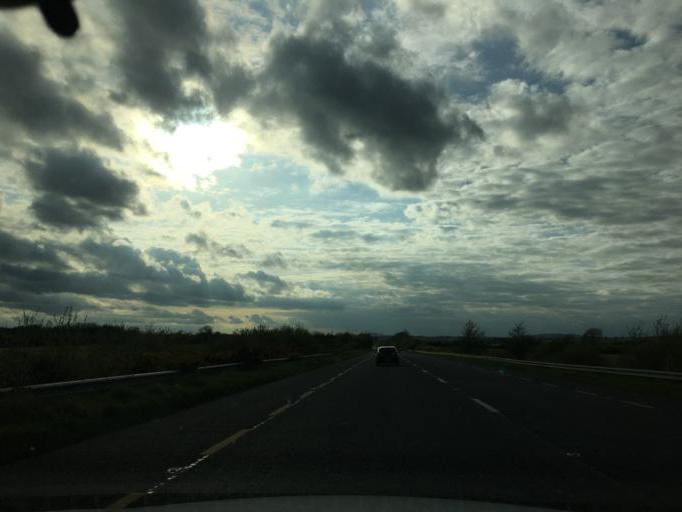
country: IE
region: Leinster
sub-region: Loch Garman
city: Loch Garman
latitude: 52.3452
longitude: -6.5947
